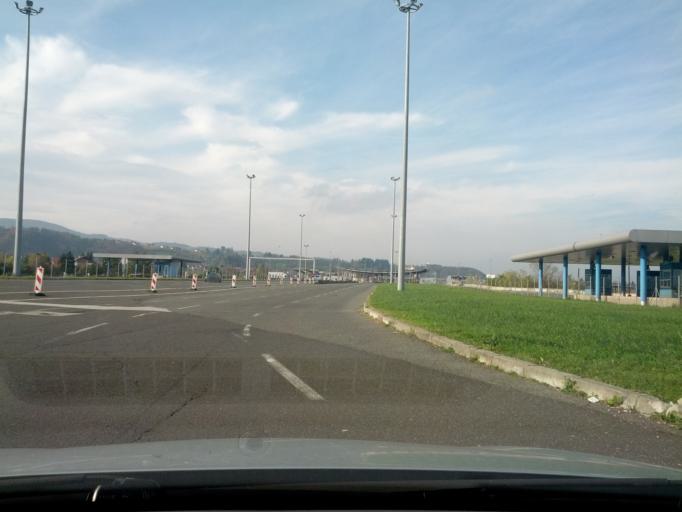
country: HR
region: Zagrebacka
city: Bregana
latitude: 45.8429
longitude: 15.6987
